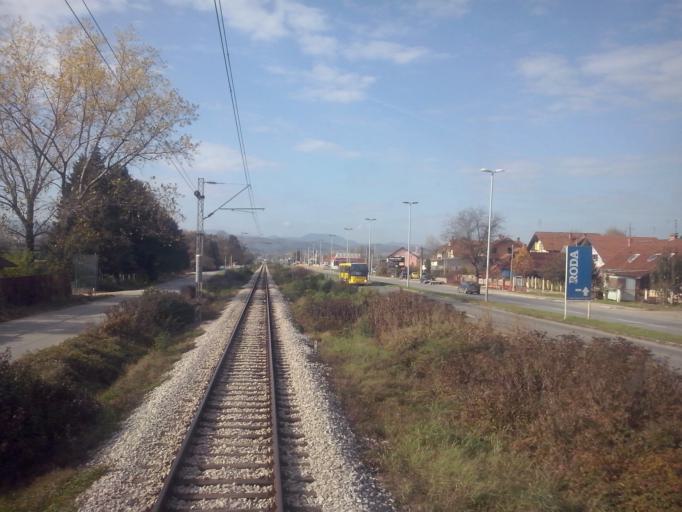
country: RS
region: Central Serbia
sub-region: Kolubarski Okrug
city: Valjevo
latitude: 44.2856
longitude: 19.9415
